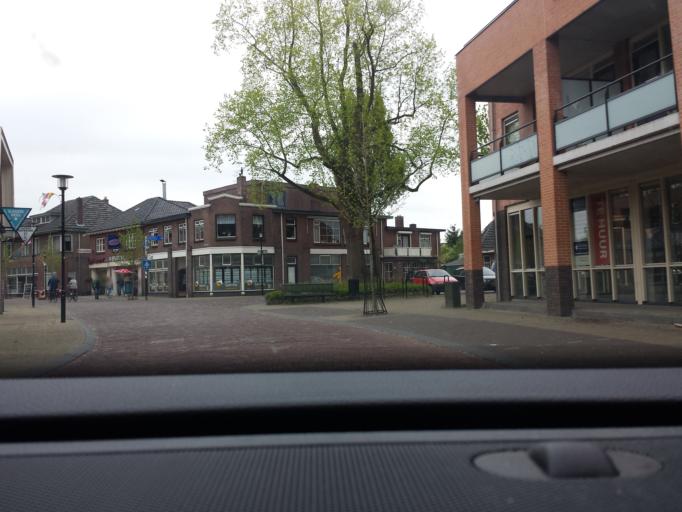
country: NL
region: Gelderland
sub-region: Gemeente Bronckhorst
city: Hengelo
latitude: 52.0519
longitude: 6.3091
